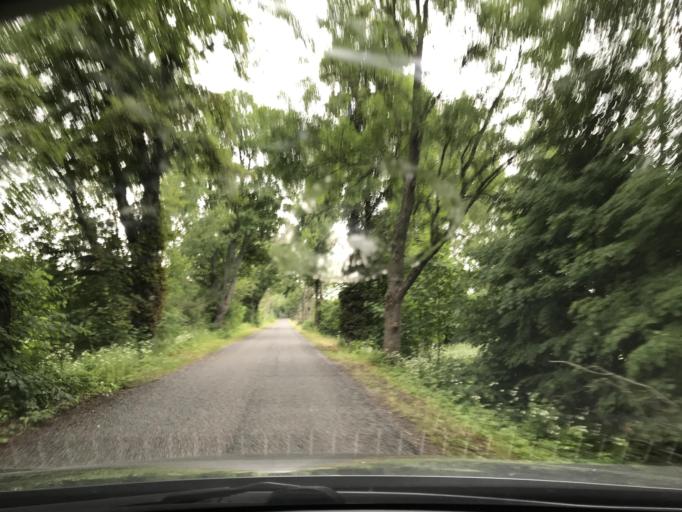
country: LV
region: Alsunga
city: Alsunga
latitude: 56.9777
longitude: 21.6389
